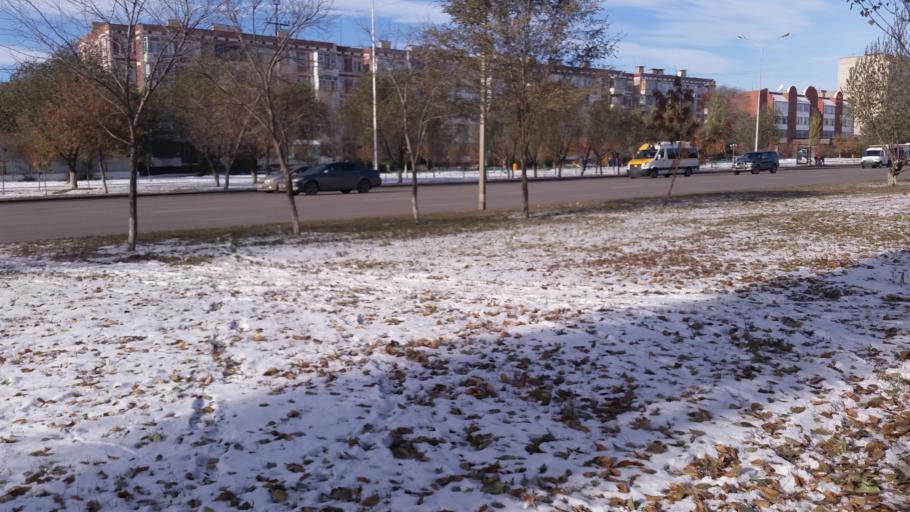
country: KZ
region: Astana Qalasy
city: Astana
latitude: 51.1538
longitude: 71.4799
